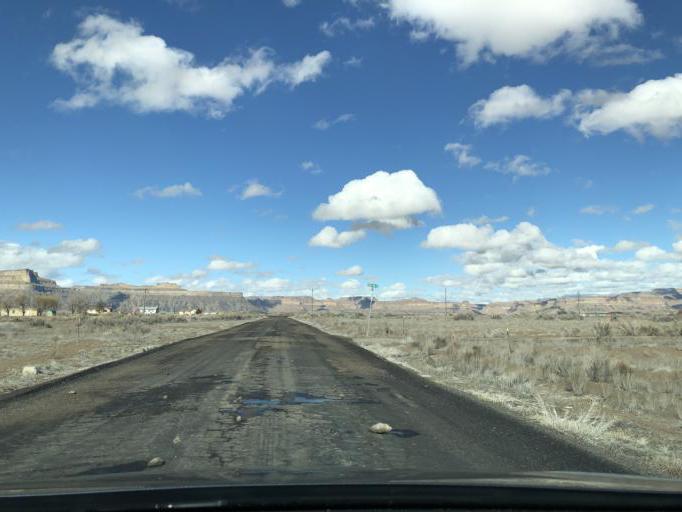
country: US
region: Utah
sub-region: Carbon County
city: East Carbon City
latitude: 38.9978
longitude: -110.1699
